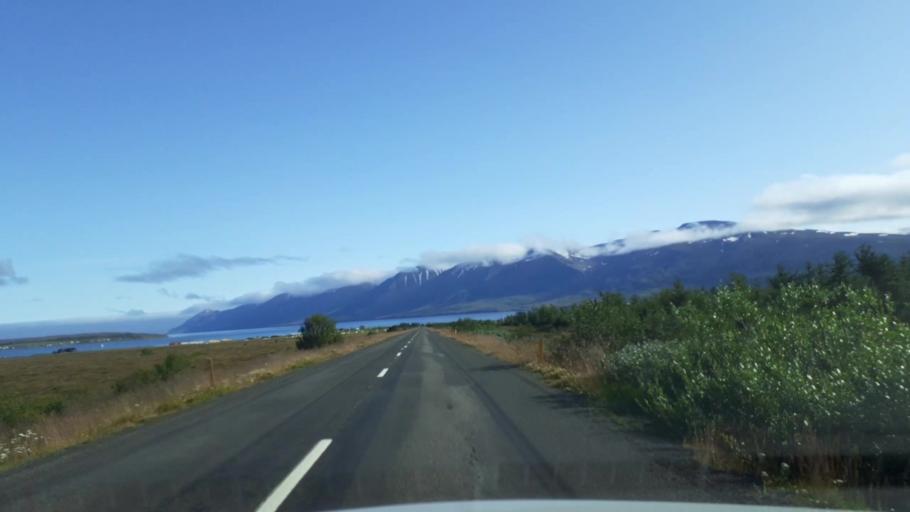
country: IS
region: Northeast
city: Dalvik
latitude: 65.9313
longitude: -18.3614
